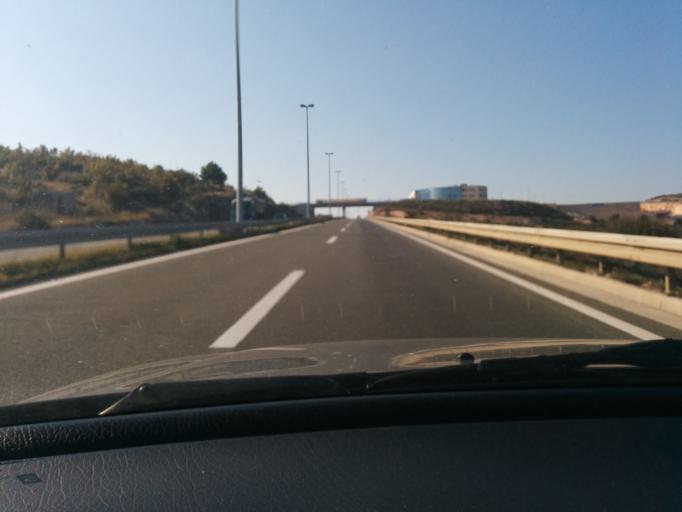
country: HR
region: Splitsko-Dalmatinska
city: Dugopolje
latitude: 43.5866
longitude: 16.5663
